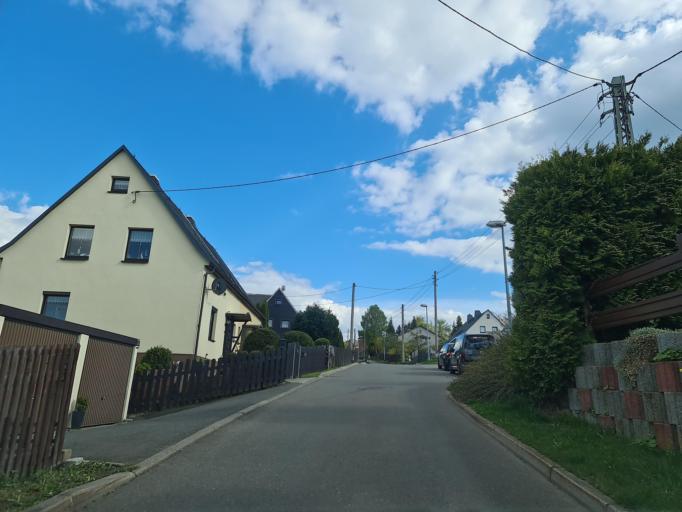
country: DE
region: Saxony
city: Ellefeld
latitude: 50.4713
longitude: 12.3888
